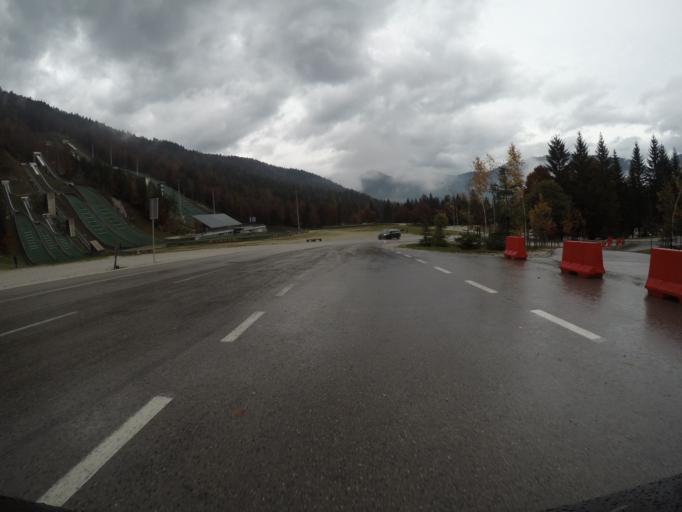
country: SI
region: Kranjska Gora
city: Kranjska Gora
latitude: 46.4769
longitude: 13.7242
